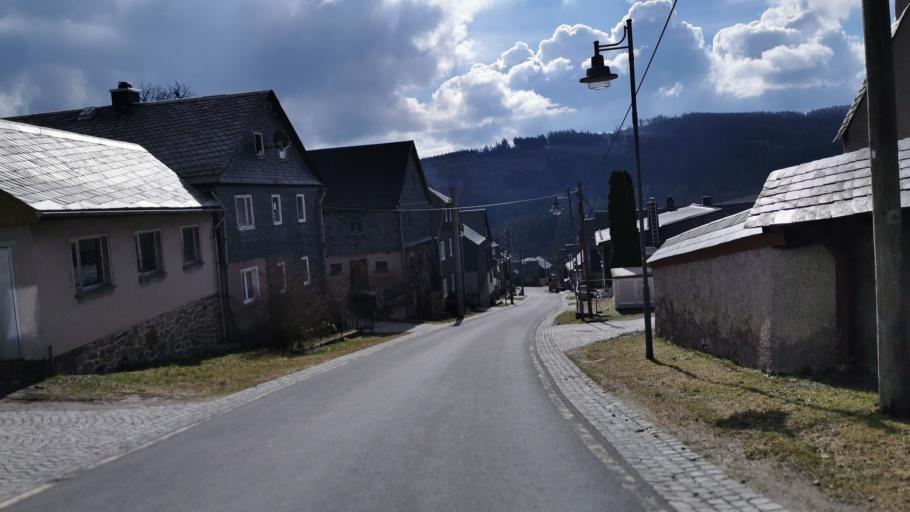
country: DE
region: Thuringia
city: Wurzbach
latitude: 50.4928
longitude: 11.4795
